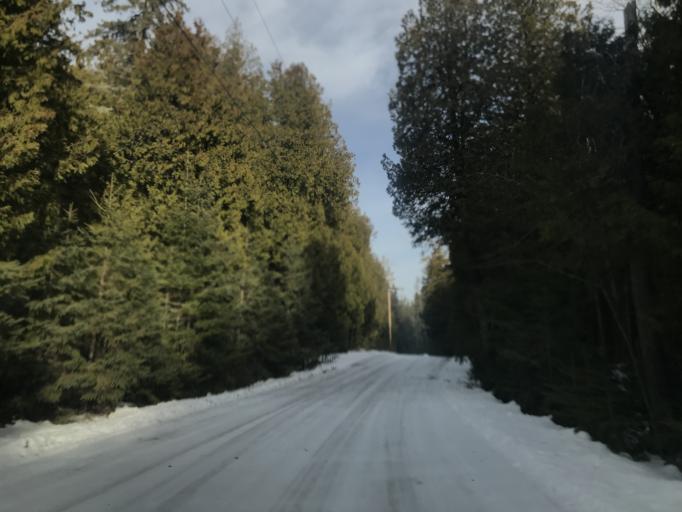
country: US
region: Wisconsin
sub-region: Door County
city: Sturgeon Bay
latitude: 45.1393
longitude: -87.0439
